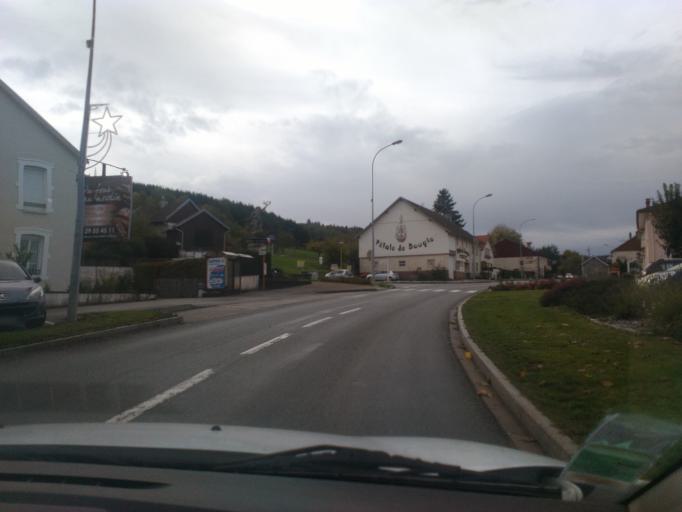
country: FR
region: Lorraine
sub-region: Departement des Vosges
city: Anould
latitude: 48.1497
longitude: 6.9213
